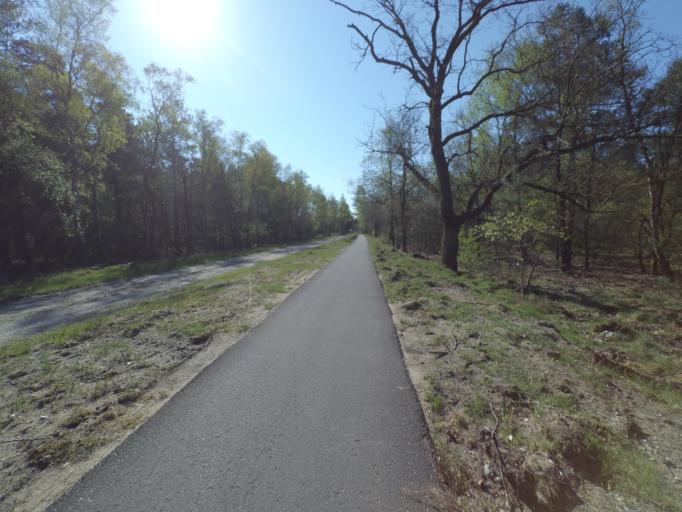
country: NL
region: Gelderland
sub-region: Gemeente Apeldoorn
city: Uddel
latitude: 52.1870
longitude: 5.8093
